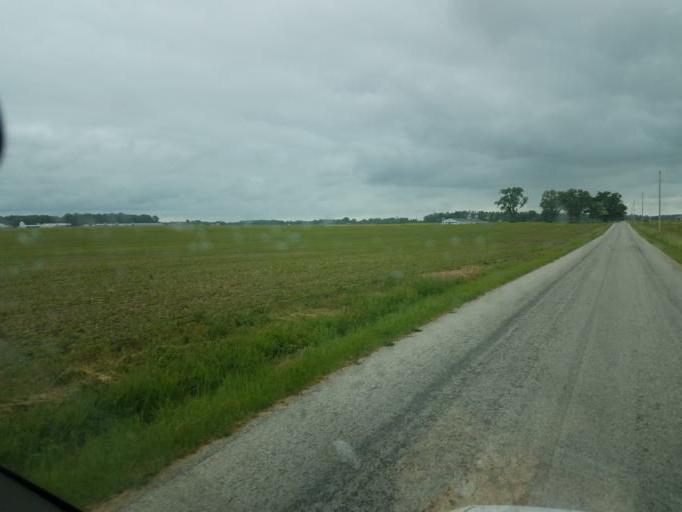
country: US
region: Ohio
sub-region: Morrow County
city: Cardington
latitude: 40.5422
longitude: -82.9005
